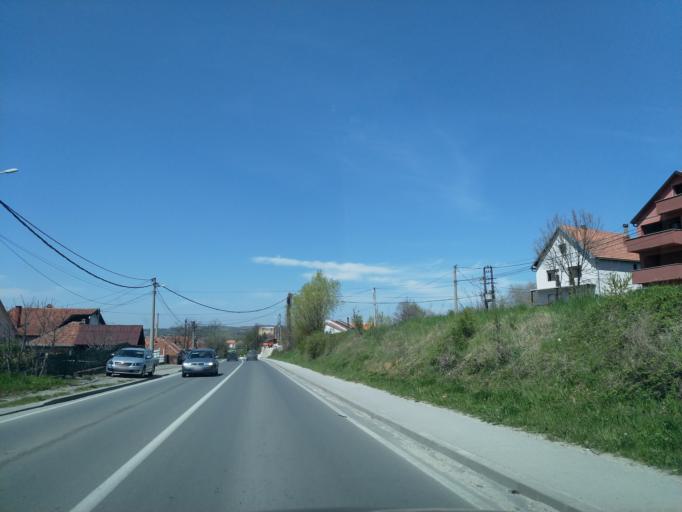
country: RS
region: Central Serbia
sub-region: Sumadijski Okrug
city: Arangelovac
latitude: 44.3204
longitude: 20.5385
